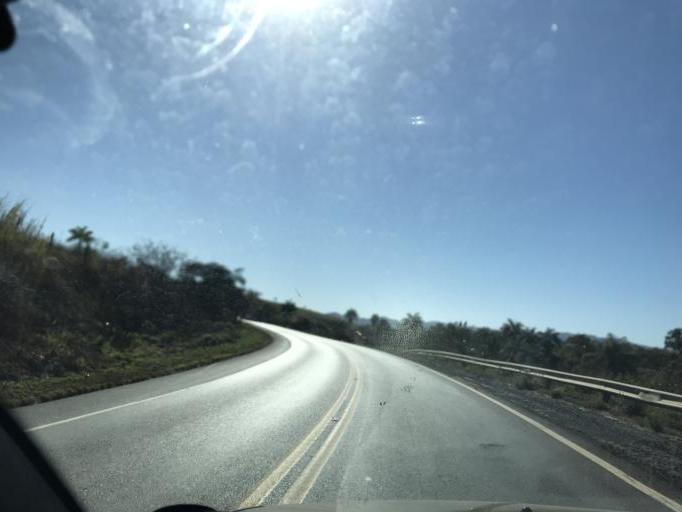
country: BR
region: Minas Gerais
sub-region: Bambui
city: Bambui
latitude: -19.8410
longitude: -45.9994
